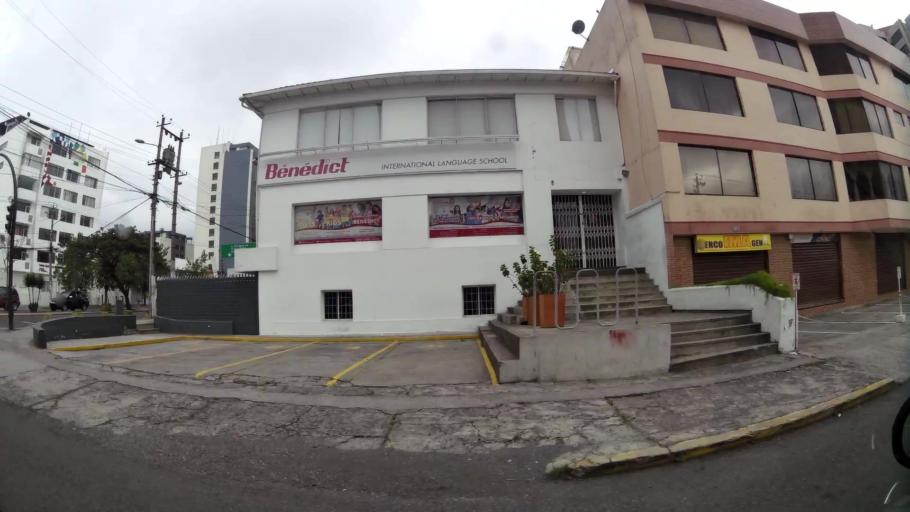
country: EC
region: Pichincha
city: Quito
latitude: -0.1962
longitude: -78.4931
